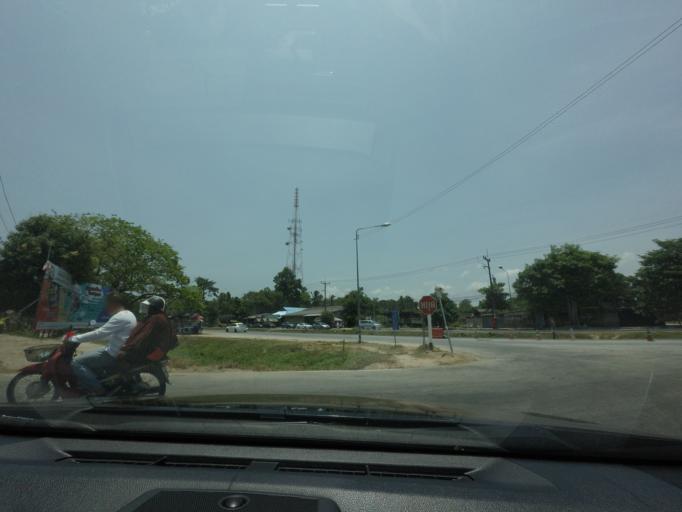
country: TH
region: Pattani
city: Yaring
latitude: 6.8617
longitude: 101.3682
